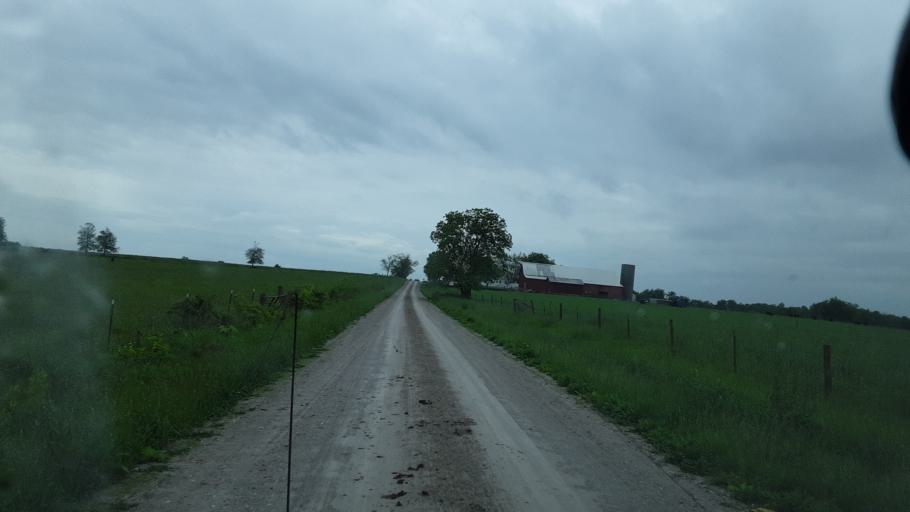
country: US
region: Missouri
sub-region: Randolph County
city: Moberly
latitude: 39.3136
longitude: -92.3050
